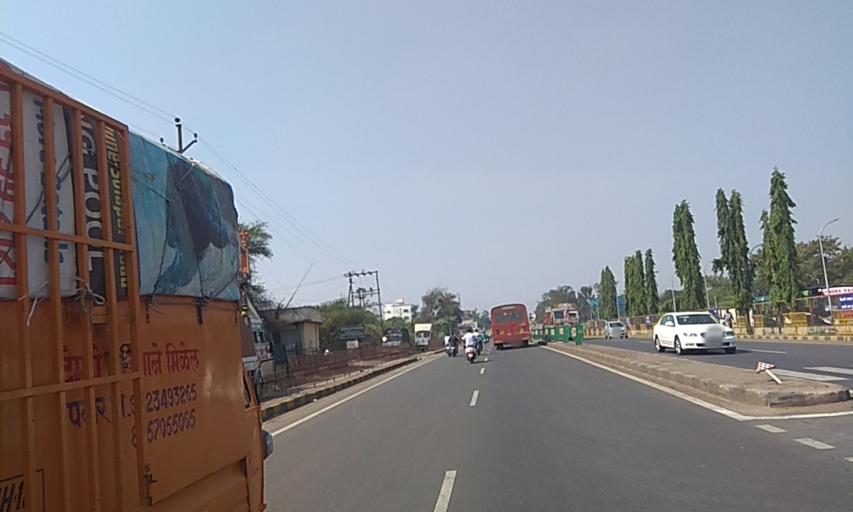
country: IN
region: Maharashtra
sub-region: Pune Division
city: Lohogaon
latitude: 18.4904
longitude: 74.0126
